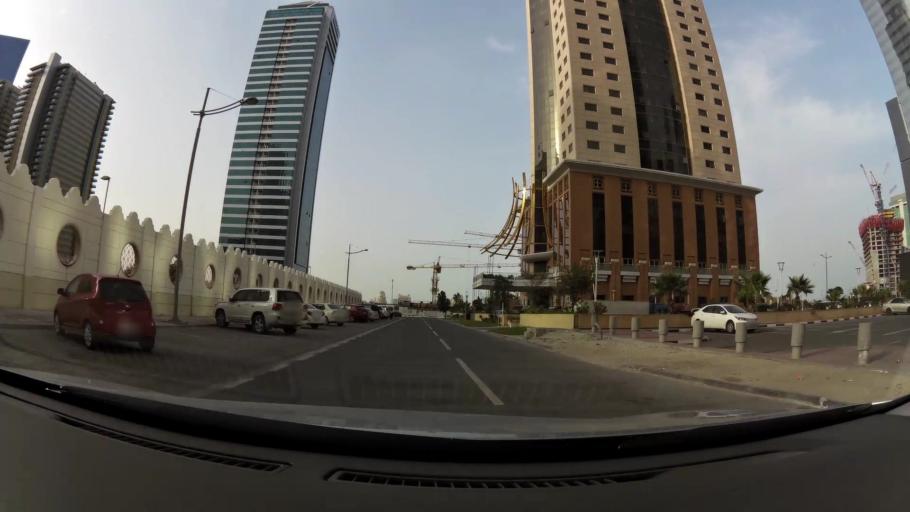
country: QA
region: Baladiyat ad Dawhah
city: Doha
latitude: 25.3286
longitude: 51.5287
